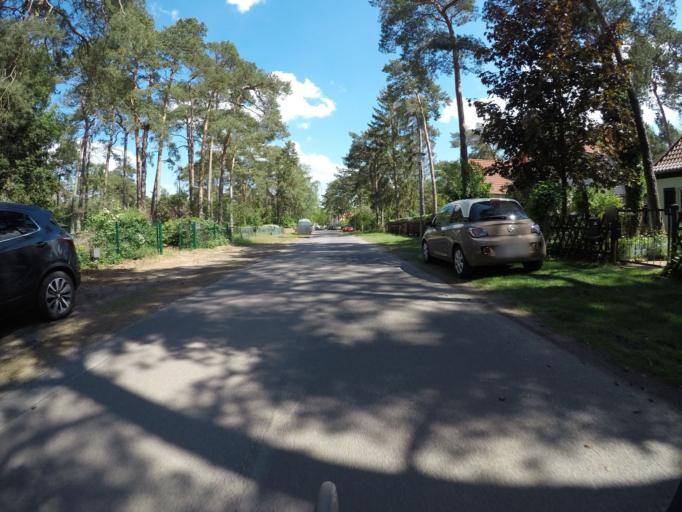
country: DE
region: Brandenburg
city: Werder
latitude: 52.3875
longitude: 12.9482
